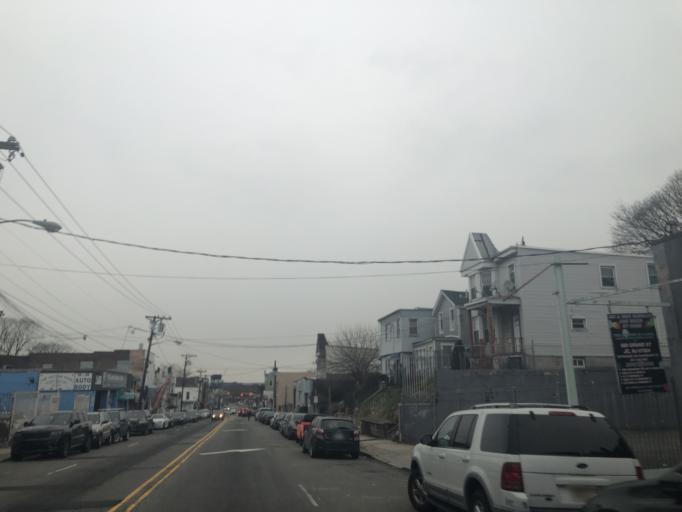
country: US
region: New Jersey
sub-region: Hudson County
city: Jersey City
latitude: 40.7201
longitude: -74.0794
